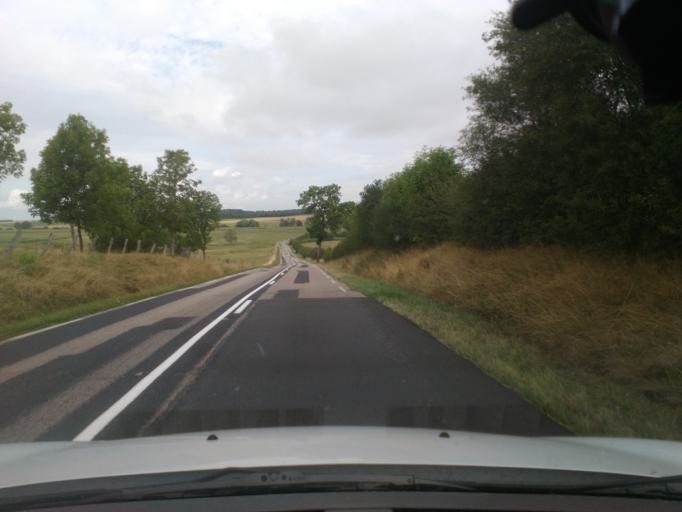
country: FR
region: Lorraine
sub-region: Departement de Meurthe-et-Moselle
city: Vezelise
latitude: 48.4259
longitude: 6.1263
